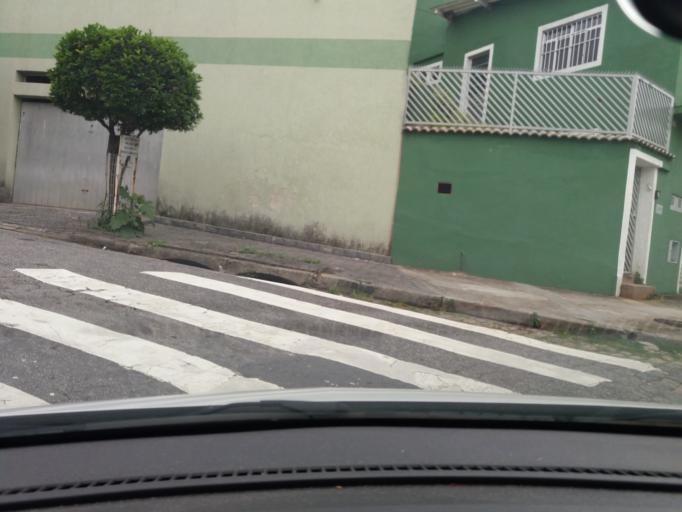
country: BR
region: Sao Paulo
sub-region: Sao Paulo
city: Sao Paulo
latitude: -23.4820
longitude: -46.6208
